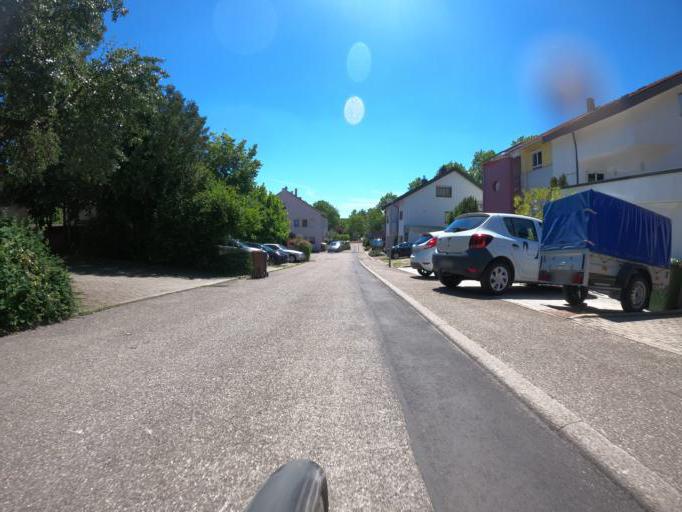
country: DE
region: Baden-Wuerttemberg
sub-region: Regierungsbezirk Stuttgart
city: Vaihingen an der Enz
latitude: 48.9360
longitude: 8.9613
